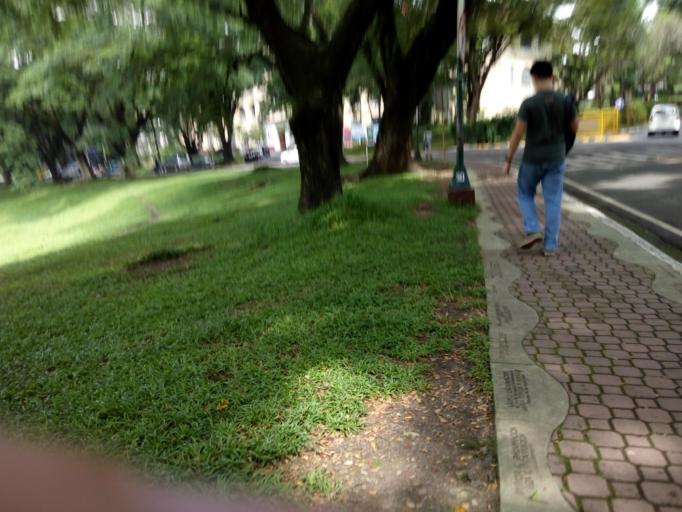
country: PH
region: Metro Manila
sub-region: Quezon City
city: Quezon City
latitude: 14.6558
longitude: 121.0730
